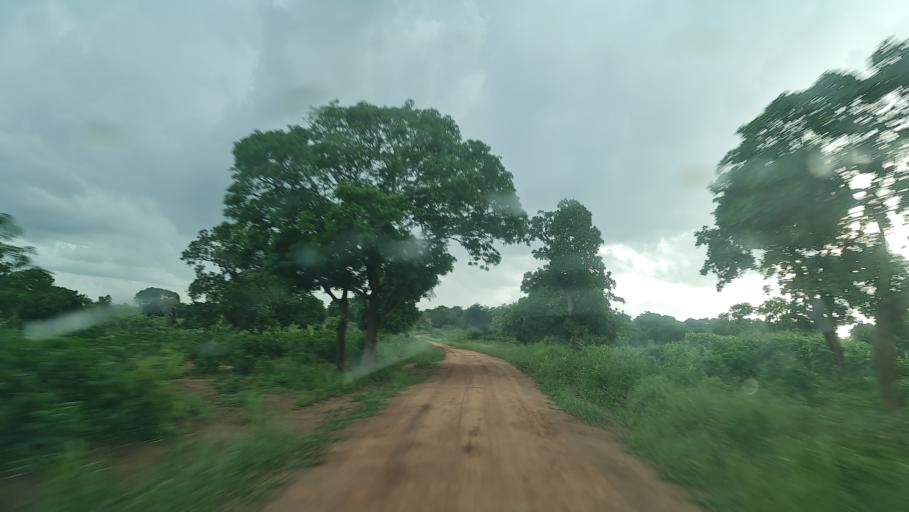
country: MZ
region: Nampula
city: Nacala
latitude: -13.9975
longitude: 40.3627
